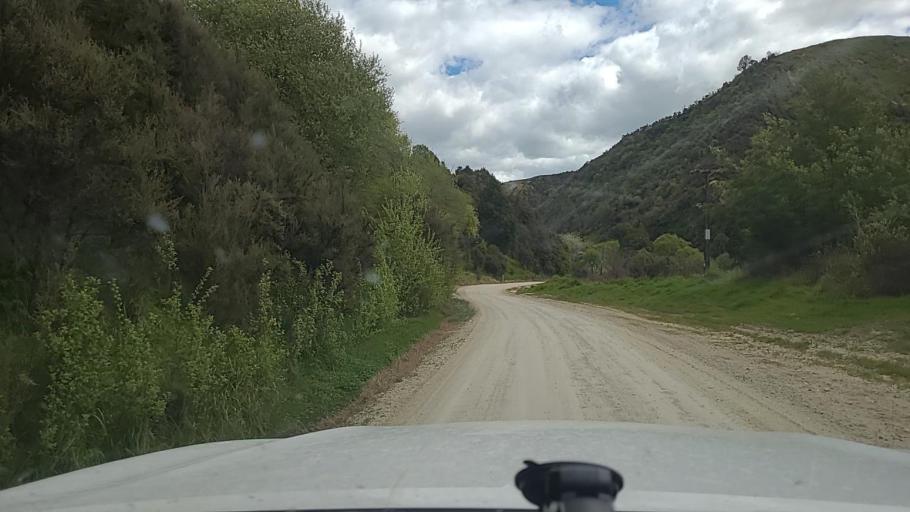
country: NZ
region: Gisborne
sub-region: Gisborne District
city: Gisborne
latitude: -38.8324
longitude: 177.7161
